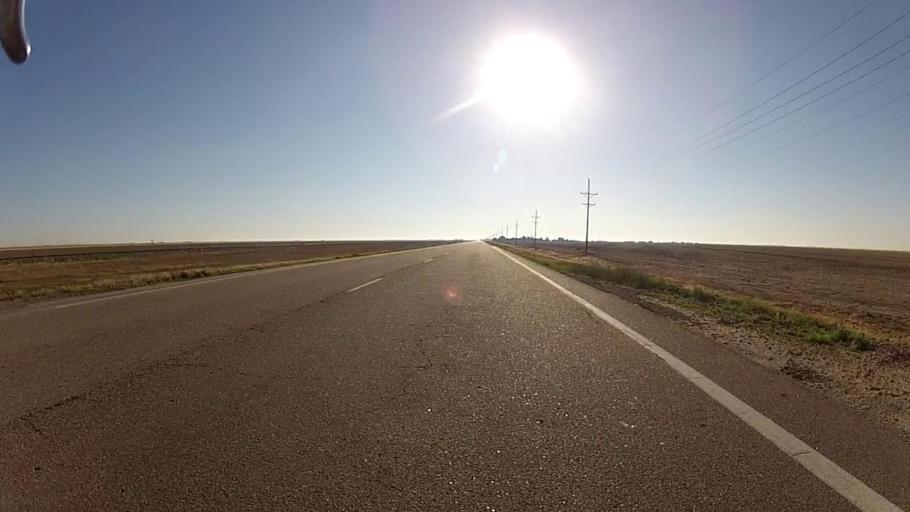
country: US
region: Kansas
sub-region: Haskell County
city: Sublette
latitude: 37.4911
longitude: -100.8164
